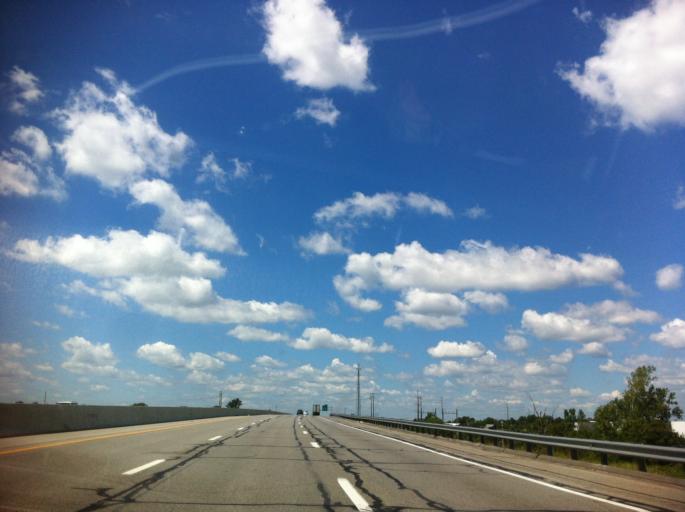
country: US
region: Ohio
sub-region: Wood County
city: Rossford
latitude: 41.5536
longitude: -83.5515
